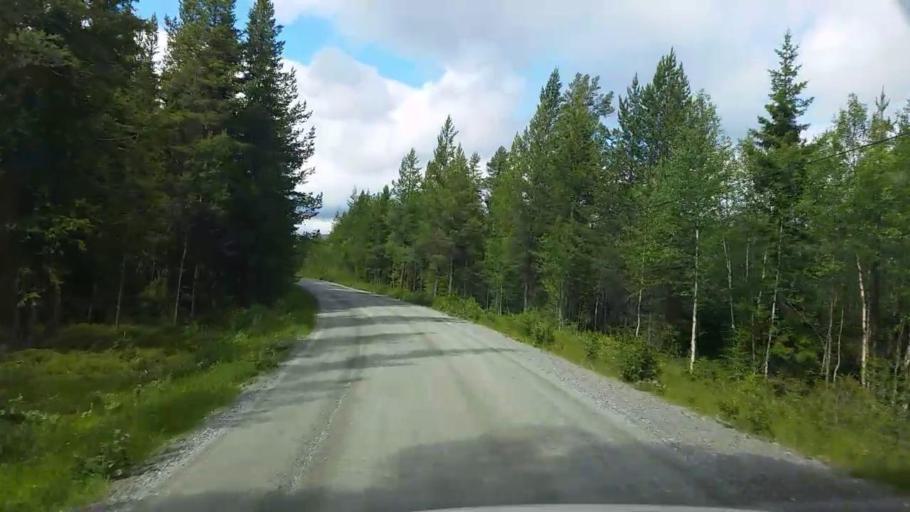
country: NO
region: Hedmark
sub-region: Engerdal
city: Engerdal
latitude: 62.4182
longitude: 12.6783
